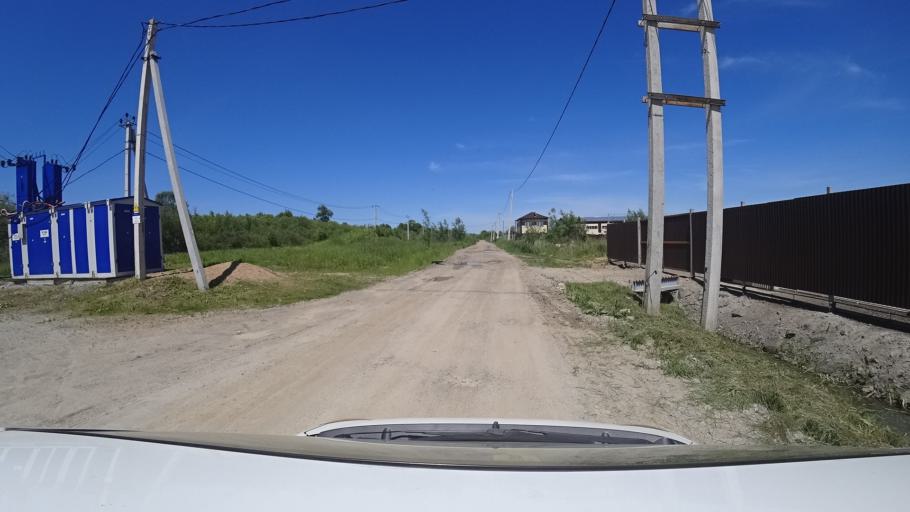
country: RU
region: Khabarovsk Krai
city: Topolevo
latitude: 48.4828
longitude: 135.1749
